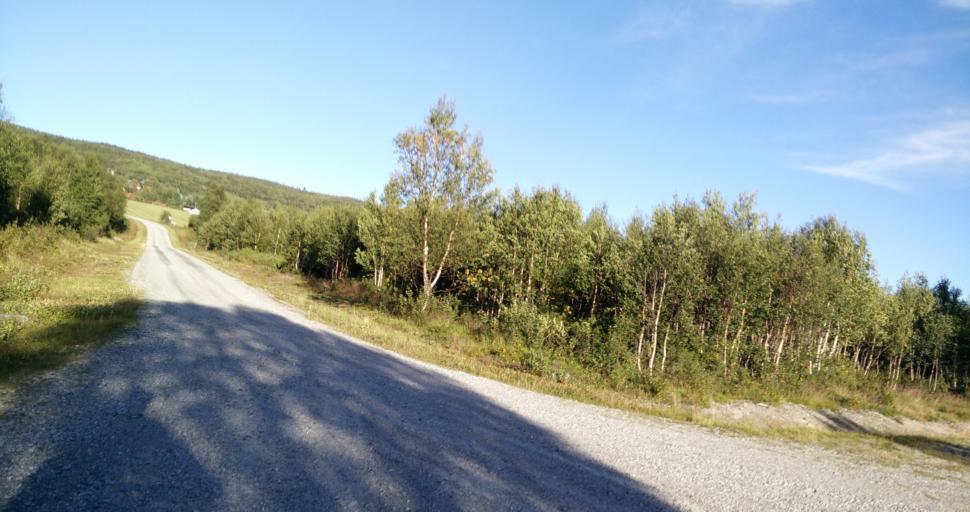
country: NO
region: Sor-Trondelag
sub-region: Tydal
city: Aas
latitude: 62.6371
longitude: 12.4279
